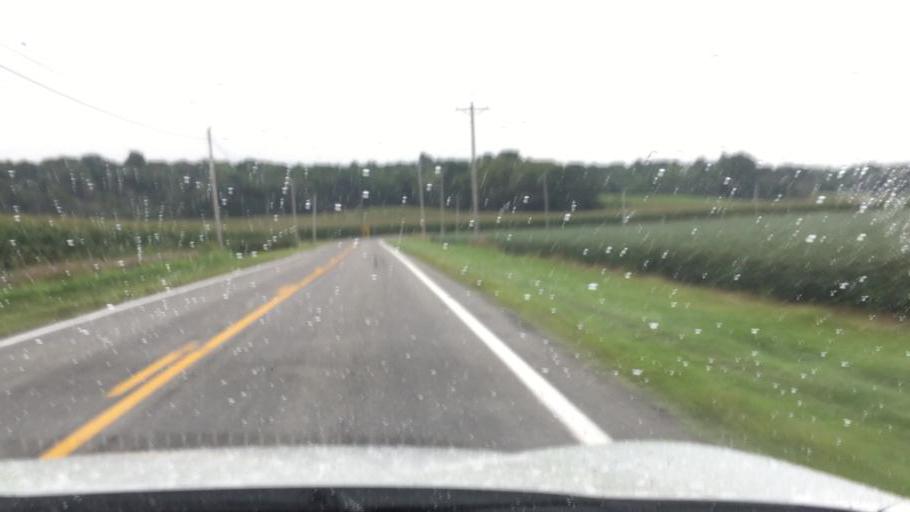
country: US
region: Ohio
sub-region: Champaign County
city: Mechanicsburg
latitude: 40.0282
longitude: -83.6422
